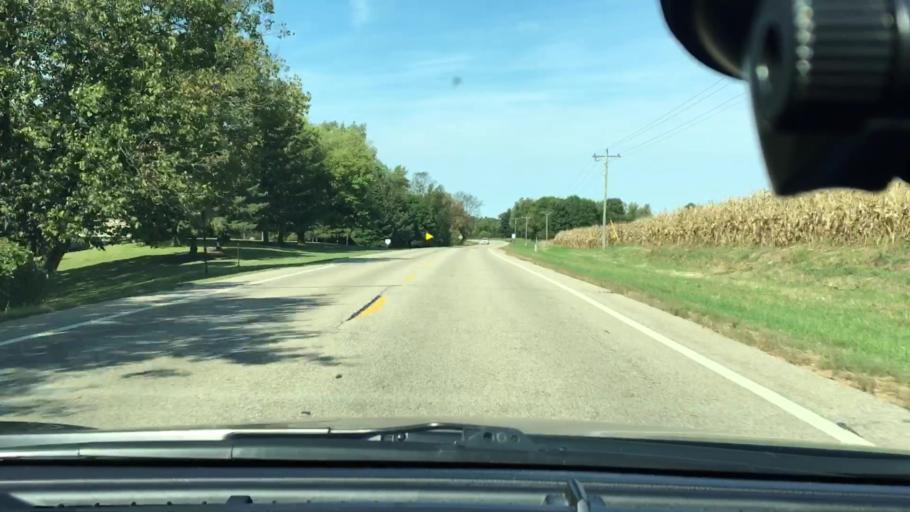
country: US
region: Minnesota
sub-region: Hennepin County
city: Corcoran
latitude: 45.0978
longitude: -93.5516
